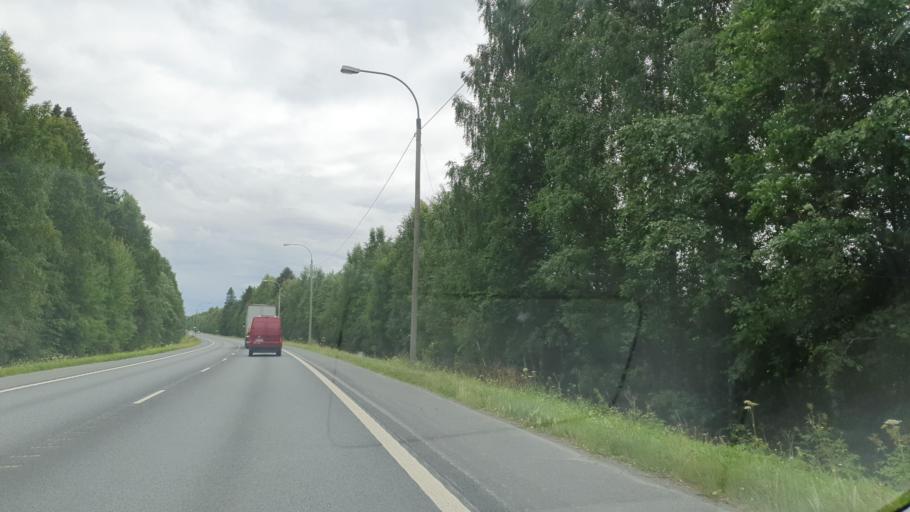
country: FI
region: Northern Savo
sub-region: Ylae-Savo
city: Iisalmi
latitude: 63.5069
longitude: 27.2580
